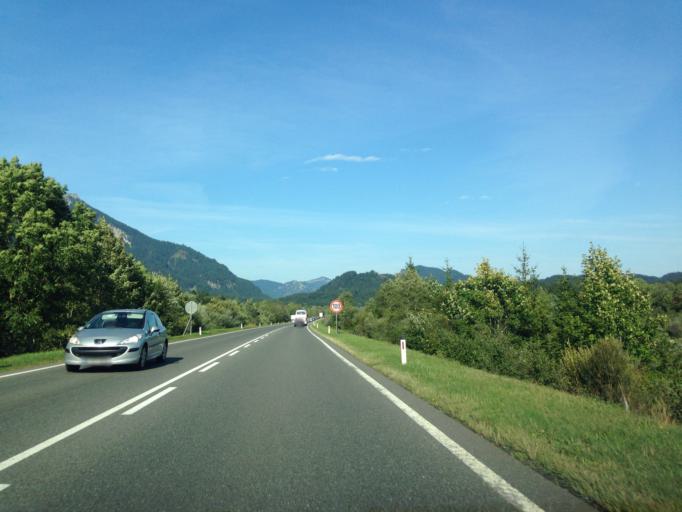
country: AT
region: Tyrol
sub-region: Politischer Bezirk Reutte
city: Pflach
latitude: 47.5265
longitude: 10.6968
